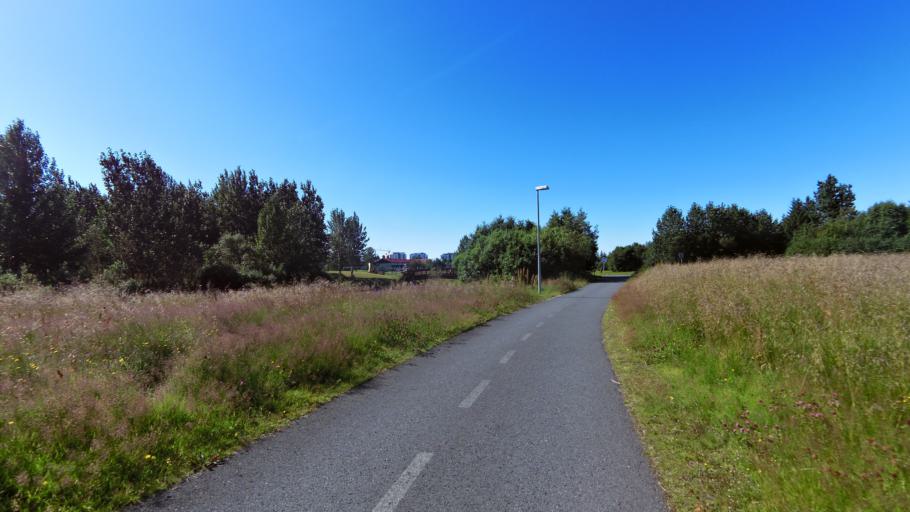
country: IS
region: Capital Region
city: Reykjavik
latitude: 64.1176
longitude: -21.8791
